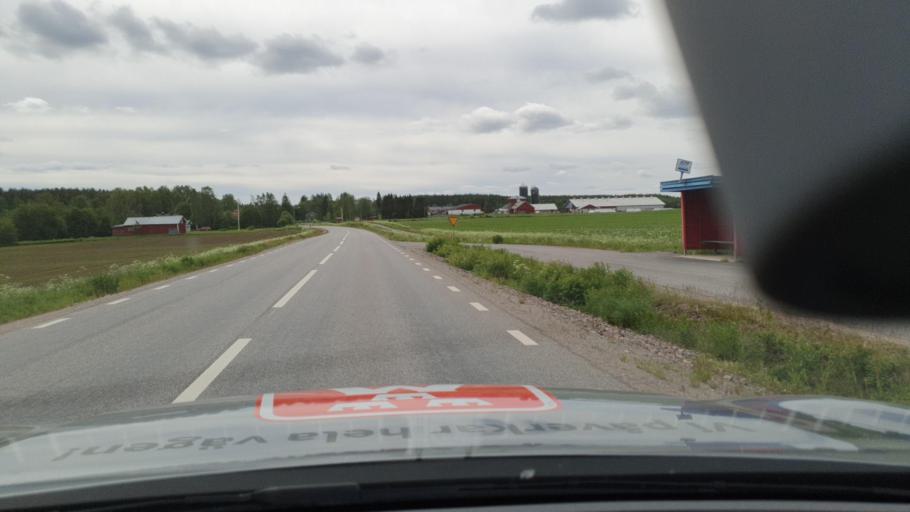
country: SE
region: Norrbotten
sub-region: Kalix Kommun
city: Kalix
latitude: 65.9248
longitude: 23.4607
